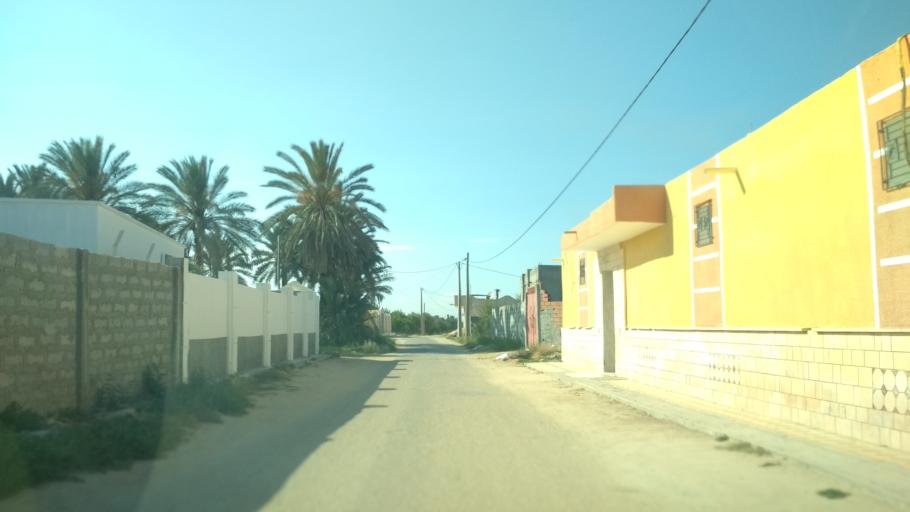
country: TN
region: Qabis
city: Gabes
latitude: 33.9497
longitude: 10.0611
